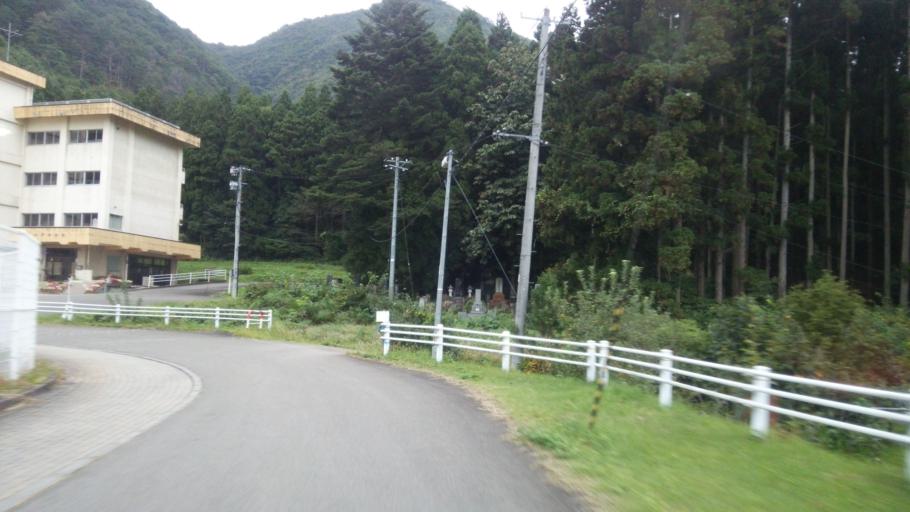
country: JP
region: Fukushima
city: Inawashiro
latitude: 37.3955
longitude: 139.9363
